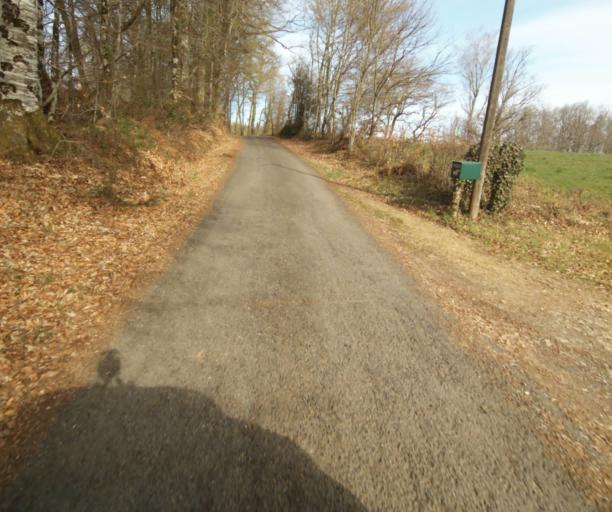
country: FR
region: Limousin
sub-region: Departement de la Correze
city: Chamboulive
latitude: 45.4174
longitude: 1.7739
